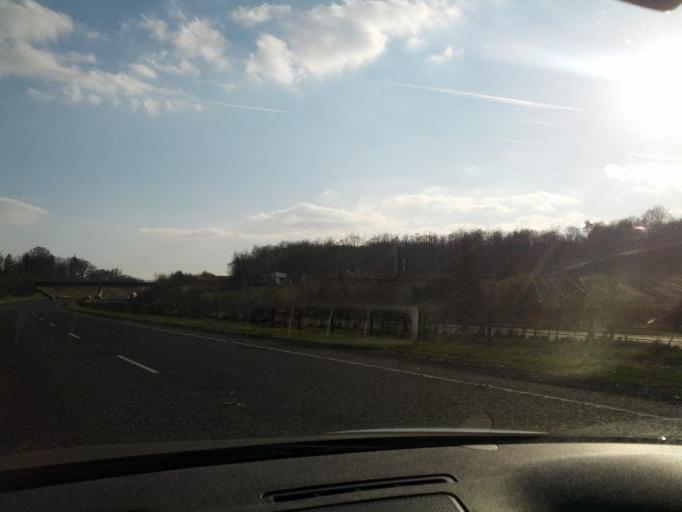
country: IE
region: Leinster
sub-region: Kildare
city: Monasterevin
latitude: 53.1251
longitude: -7.0388
